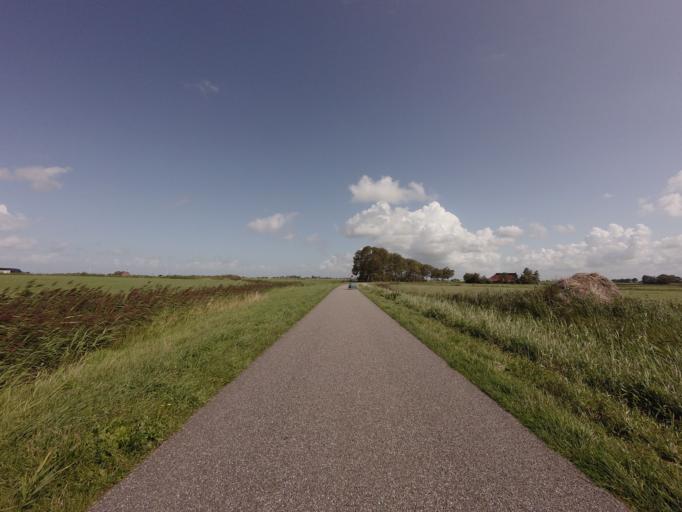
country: NL
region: Friesland
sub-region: Sudwest Fryslan
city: Makkum
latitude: 53.0636
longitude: 5.4367
